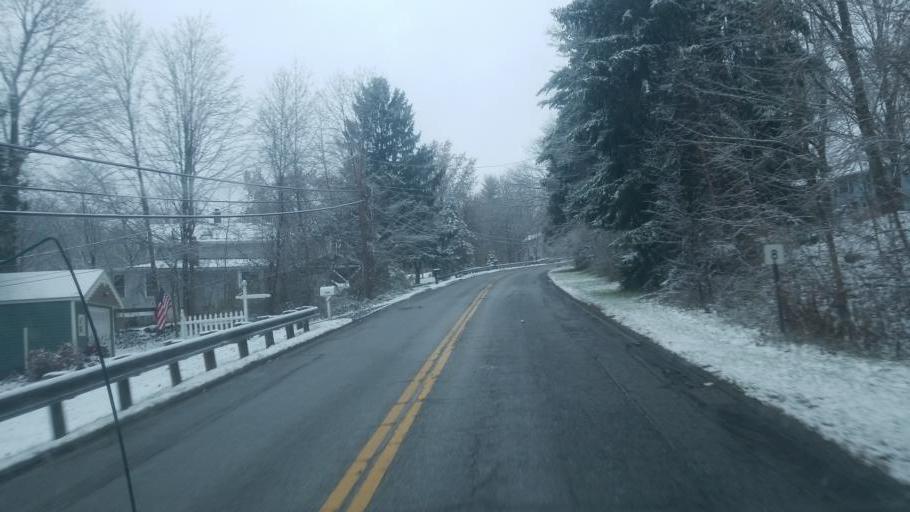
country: US
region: Ohio
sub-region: Geauga County
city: Burton
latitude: 41.4643
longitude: -81.1436
